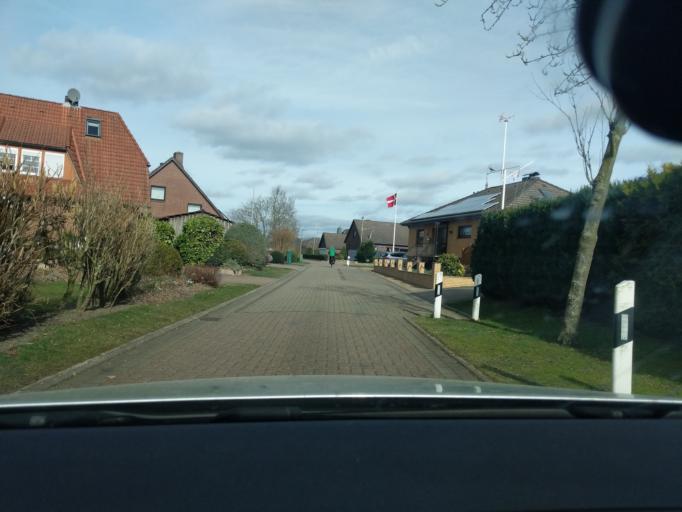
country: DE
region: Lower Saxony
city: Drochtersen
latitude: 53.6860
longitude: 9.4319
